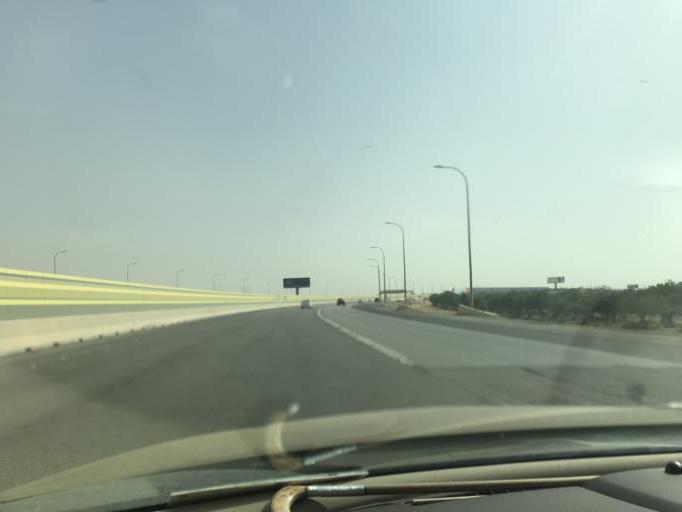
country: SA
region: Ar Riyad
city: Riyadh
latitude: 24.9182
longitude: 46.7232
